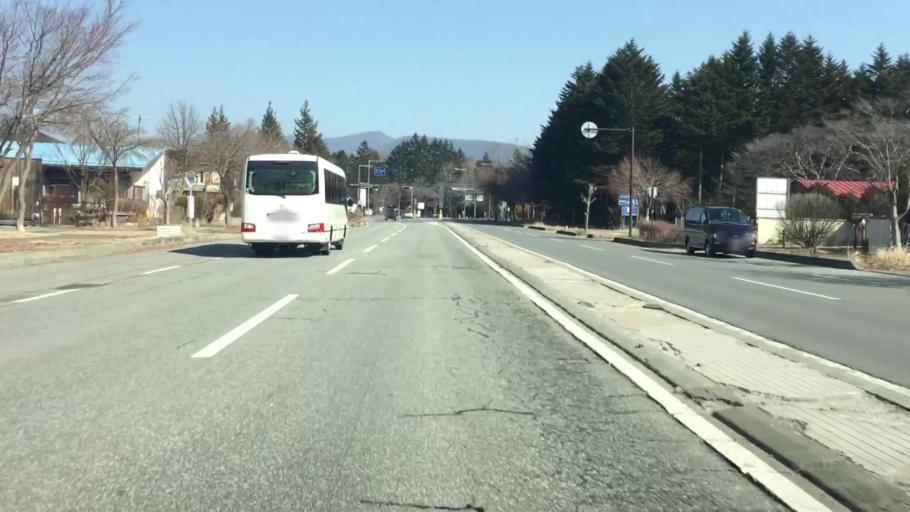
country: JP
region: Nagano
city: Saku
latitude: 36.3316
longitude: 138.6310
